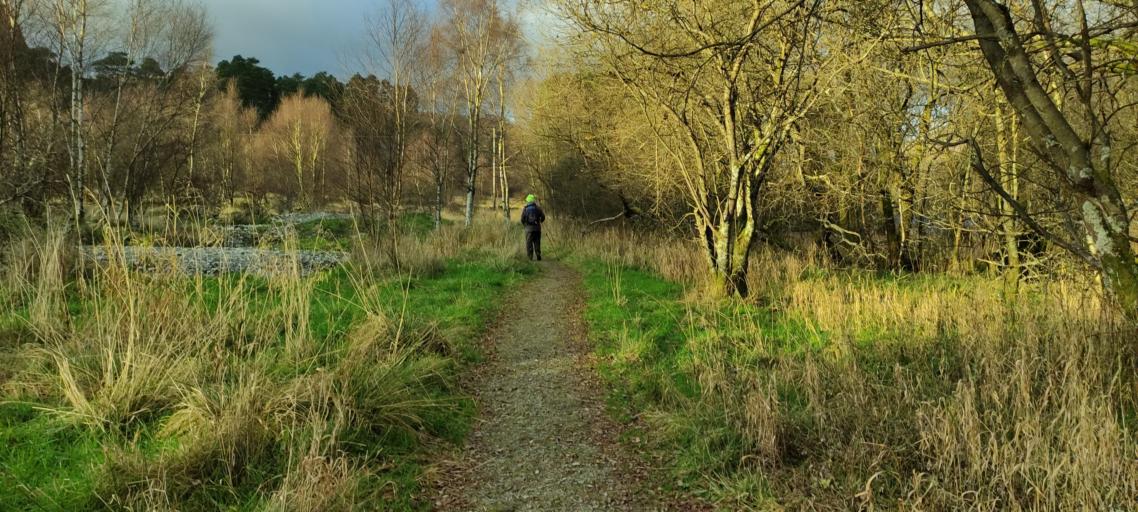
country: GB
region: England
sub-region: Cumbria
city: Ambleside
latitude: 54.5089
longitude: -3.0489
